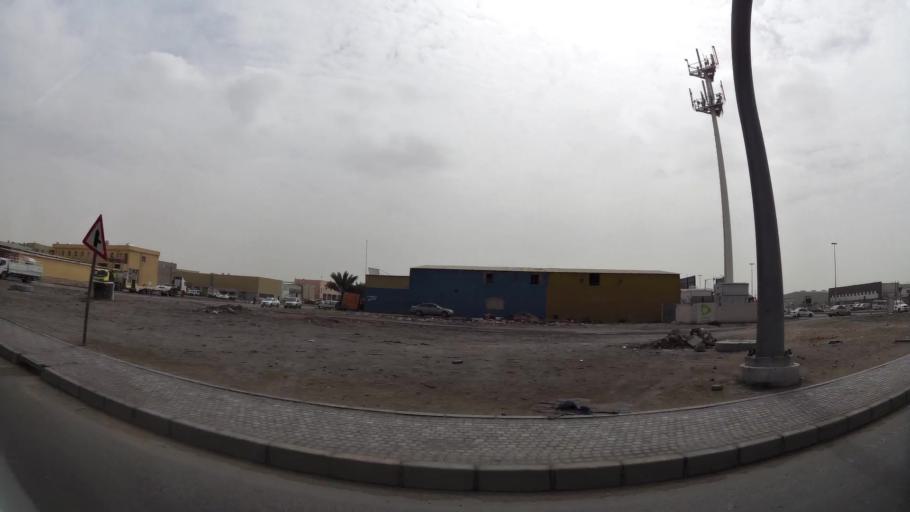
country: AE
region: Abu Dhabi
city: Abu Dhabi
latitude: 24.3596
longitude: 54.5021
